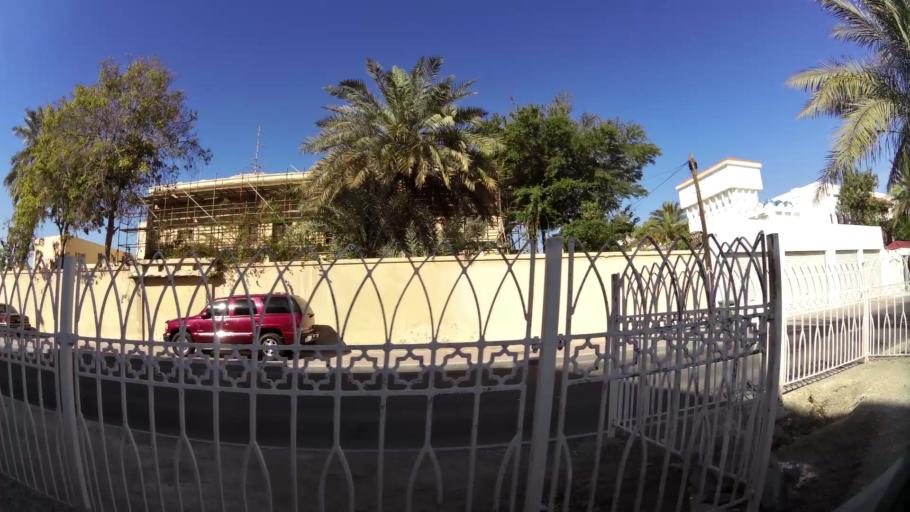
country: BH
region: Muharraq
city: Al Muharraq
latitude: 26.2566
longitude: 50.6080
